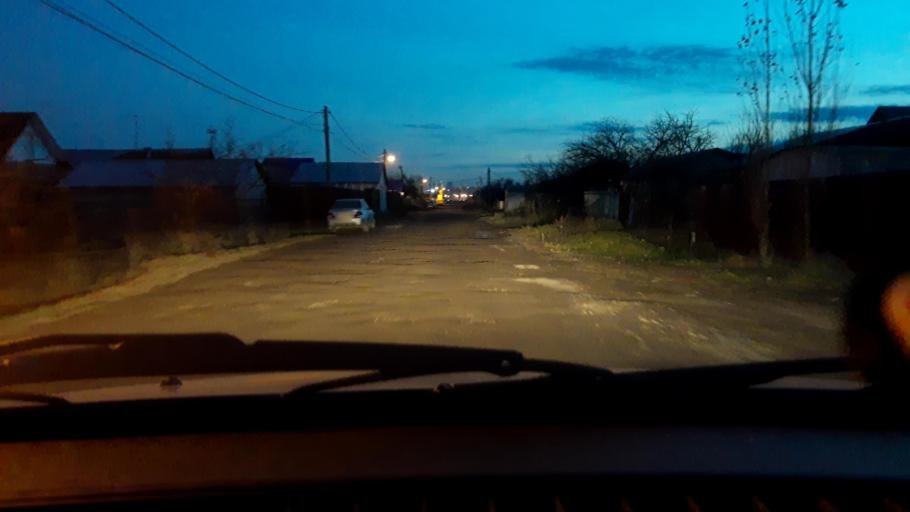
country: RU
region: Bashkortostan
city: Ufa
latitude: 54.7864
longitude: 55.9547
